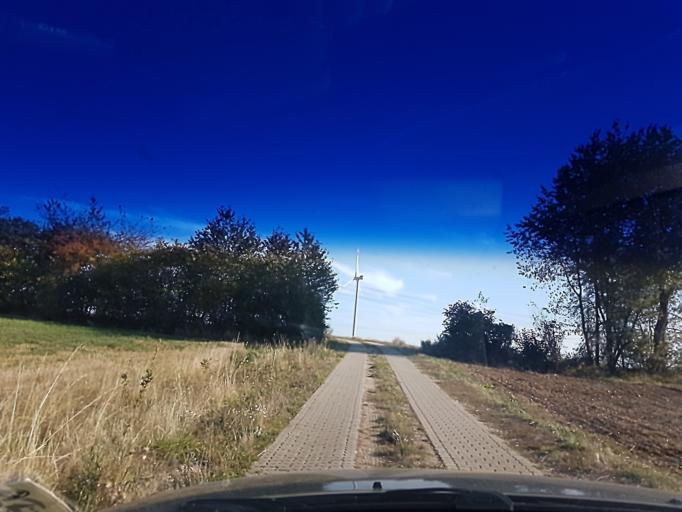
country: DE
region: Bavaria
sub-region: Upper Franconia
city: Wattendorf
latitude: 49.9853
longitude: 11.1070
